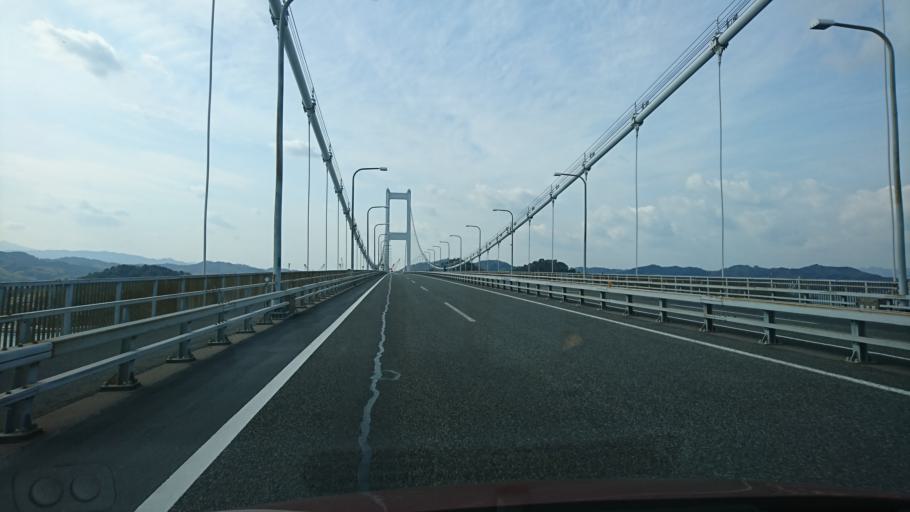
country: JP
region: Hiroshima
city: Takehara
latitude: 34.1160
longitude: 132.9867
